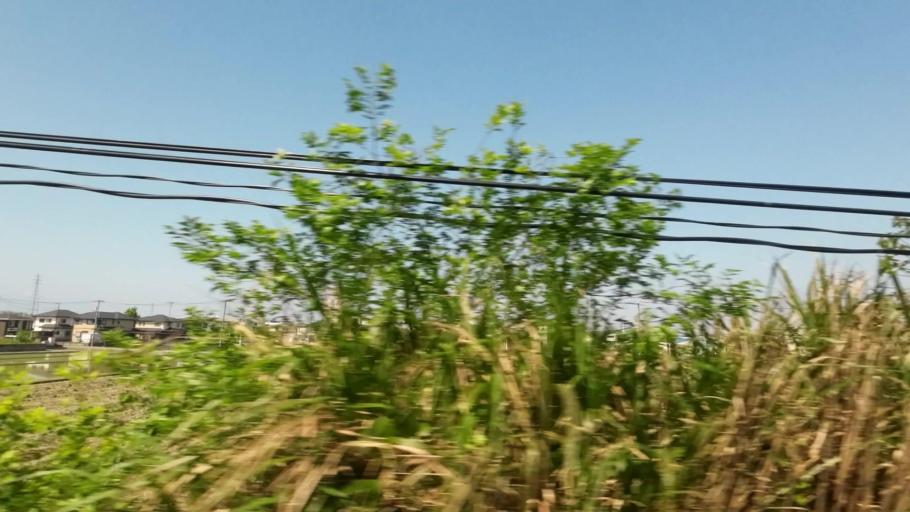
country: JP
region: Kagawa
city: Kan'onjicho
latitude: 34.1183
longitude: 133.6473
